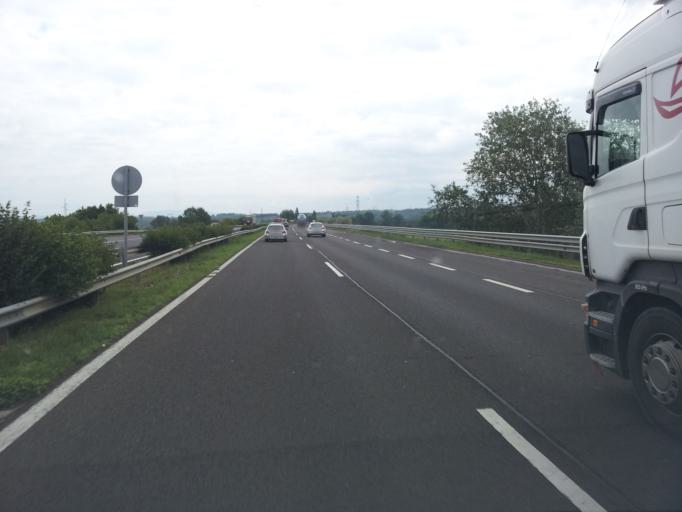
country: HU
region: Heves
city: Hatvan
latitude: 47.6840
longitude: 19.6661
